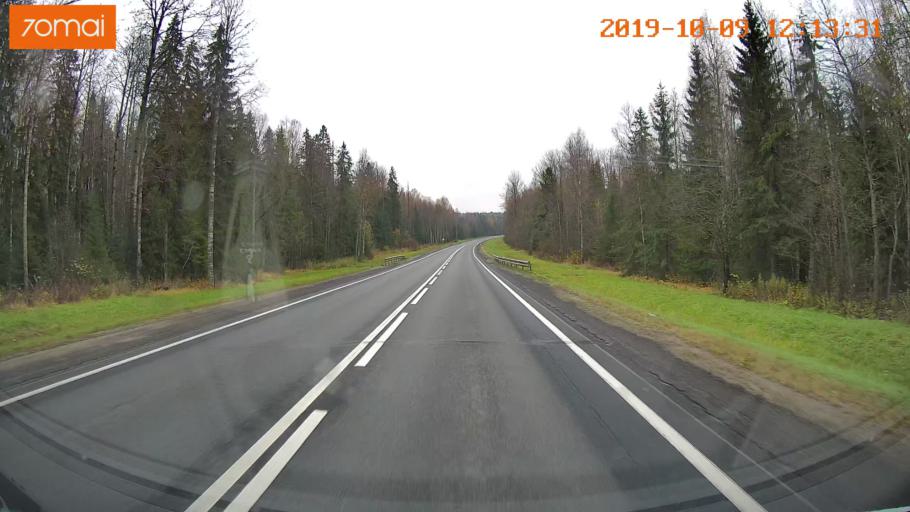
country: RU
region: Jaroslavl
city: Prechistoye
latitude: 58.5093
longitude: 40.3453
